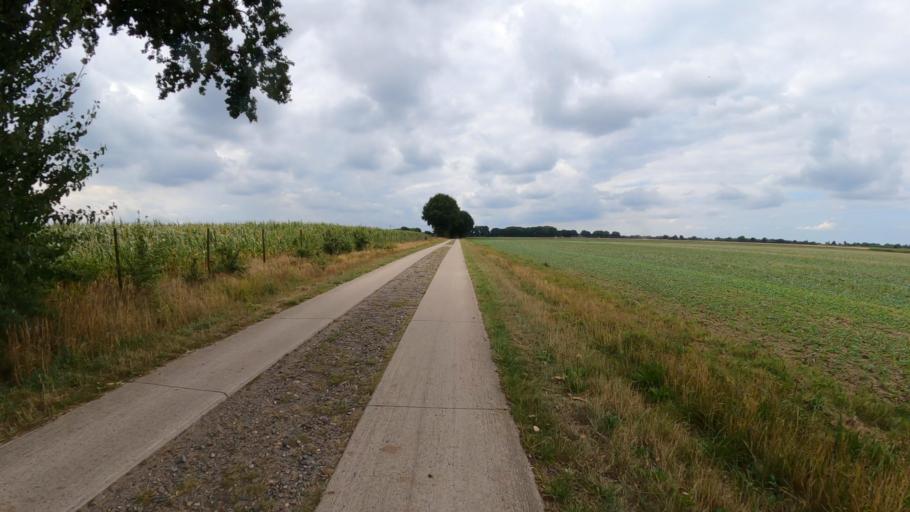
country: DE
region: Lower Saxony
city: Tostedt
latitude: 53.3003
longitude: 9.7255
